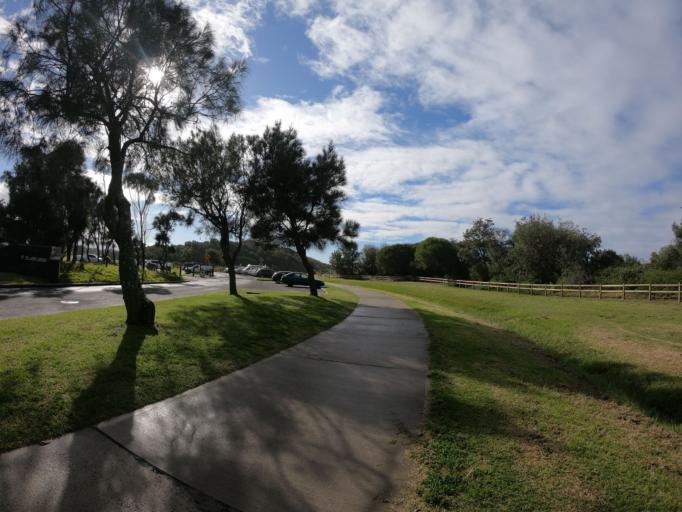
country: AU
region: New South Wales
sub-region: Wollongong
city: East Corrimal
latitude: -34.3775
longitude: 150.9192
